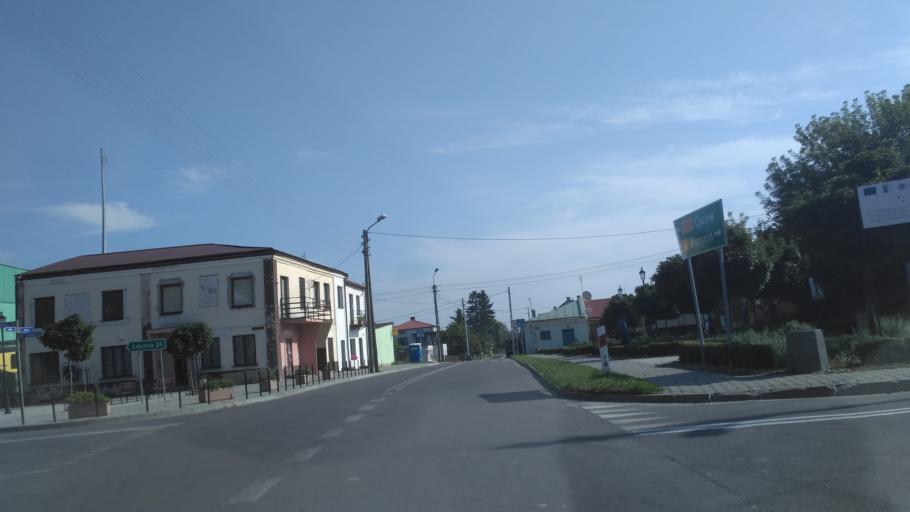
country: PL
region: Lublin Voivodeship
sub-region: Powiat leczynski
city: Cycow
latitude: 51.1945
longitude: 23.1639
